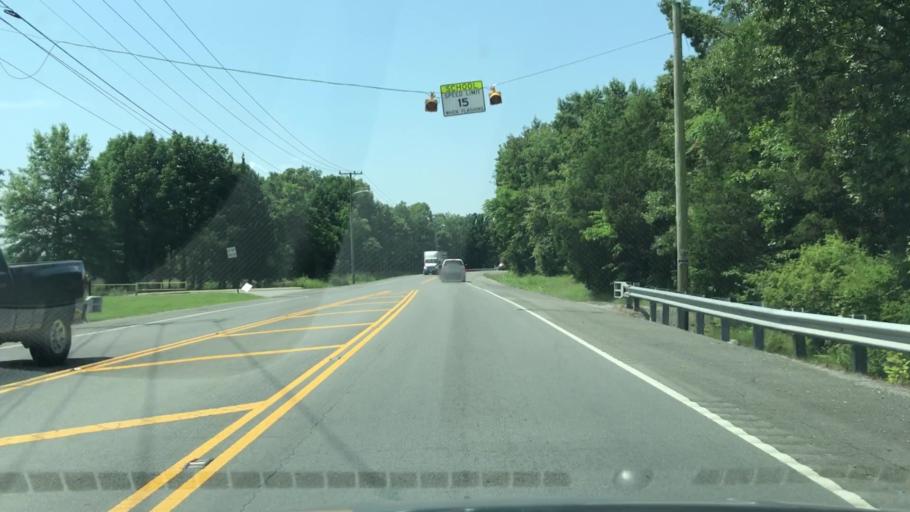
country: US
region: Tennessee
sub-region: Rutherford County
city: La Vergne
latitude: 36.0486
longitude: -86.6002
